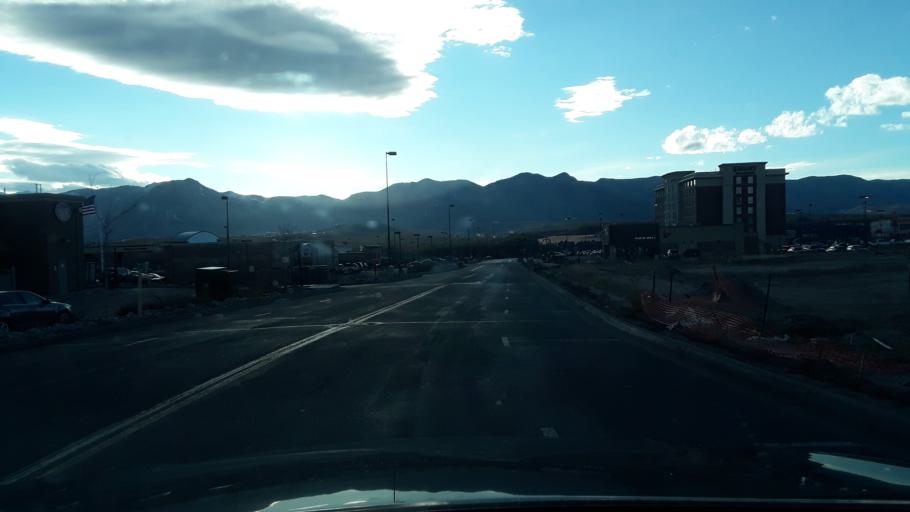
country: US
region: Colorado
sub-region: El Paso County
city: Gleneagle
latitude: 38.9920
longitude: -104.8058
